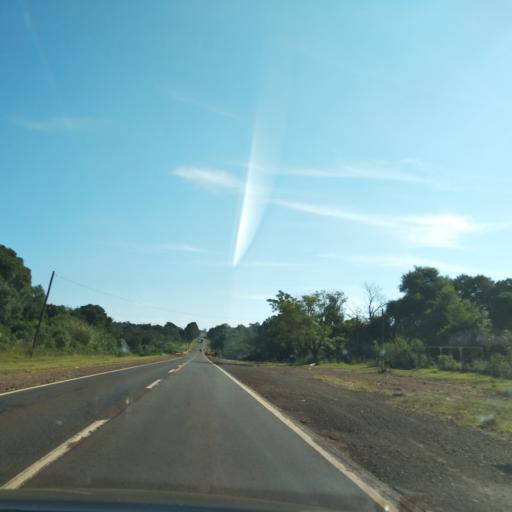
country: AR
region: Misiones
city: Santo Pipo
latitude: -27.1195
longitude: -55.3713
